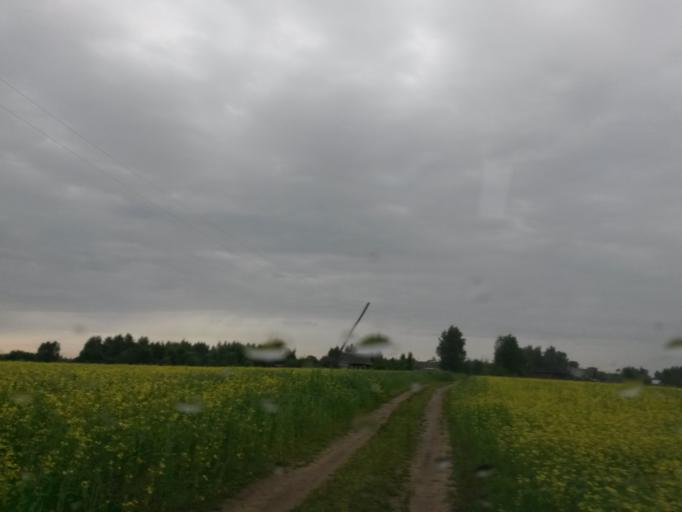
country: RU
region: Jaroslavl
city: Tutayev
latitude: 57.9430
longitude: 39.4408
